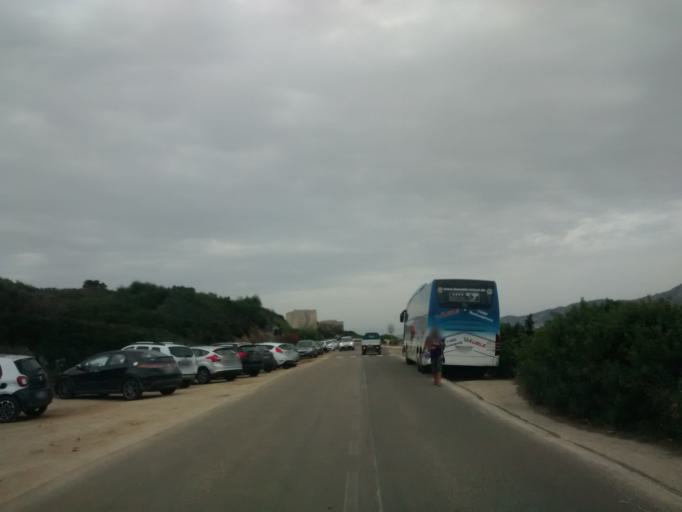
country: IT
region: Sardinia
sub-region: Provincia di Cagliari
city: Villasimius
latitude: 39.1167
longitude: 9.5077
